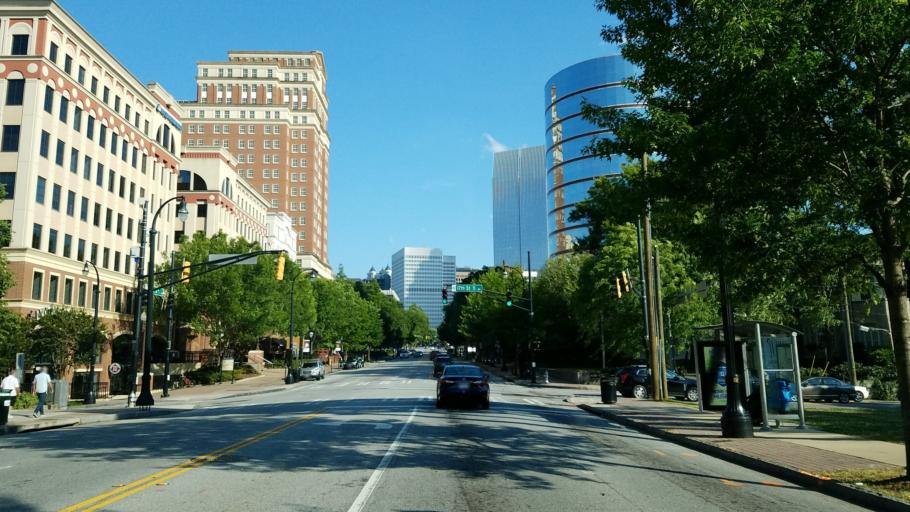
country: US
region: Georgia
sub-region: Fulton County
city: Atlanta
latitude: 33.7928
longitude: -84.3866
